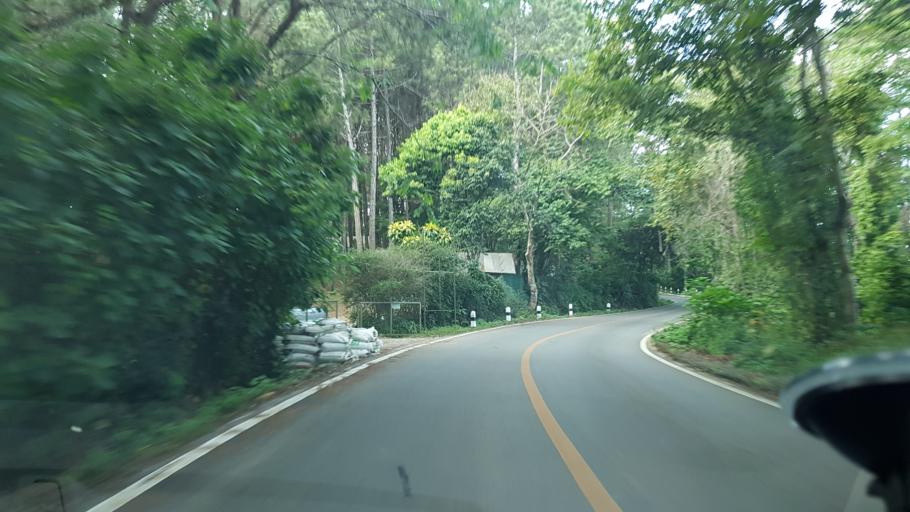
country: TH
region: Chiang Rai
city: Mae Fa Luang
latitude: 20.3319
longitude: 99.8143
